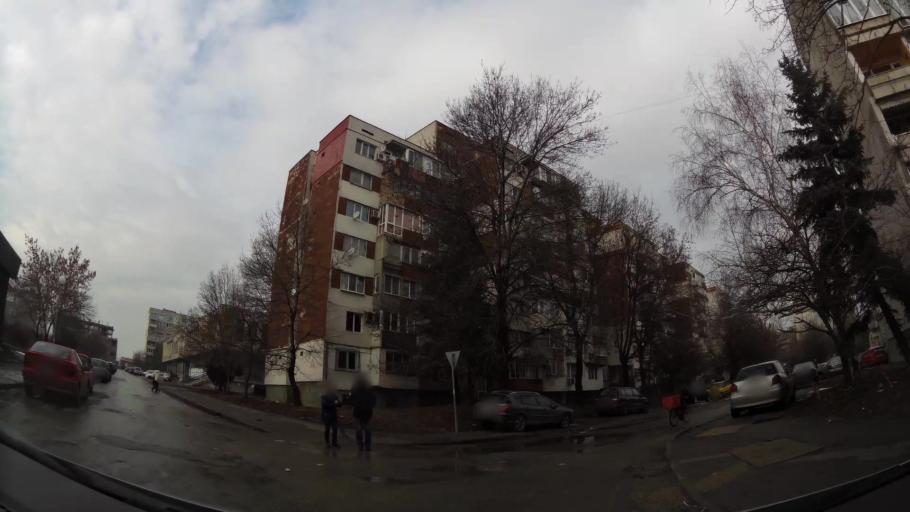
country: BG
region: Sofiya
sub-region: Obshtina Bozhurishte
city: Bozhurishte
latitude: 42.7089
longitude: 23.2510
